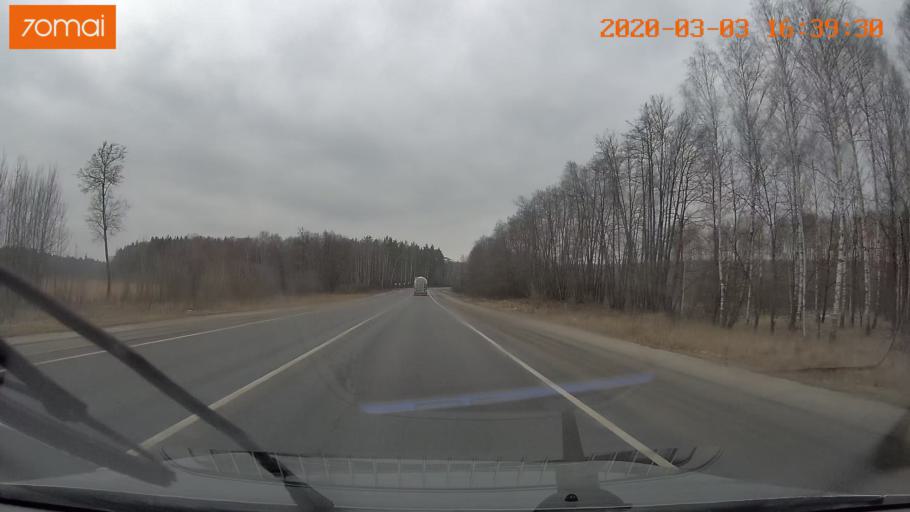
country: RU
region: Moskovskaya
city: Lopatinskiy
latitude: 55.3771
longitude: 38.7536
